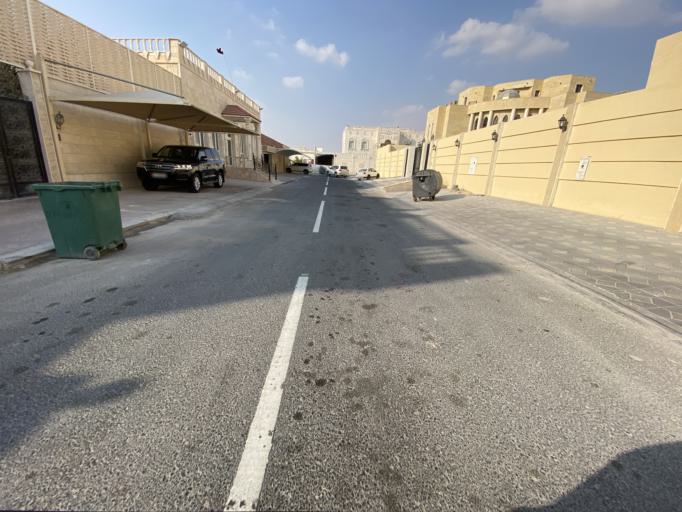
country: QA
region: Baladiyat ar Rayyan
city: Ar Rayyan
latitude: 25.2365
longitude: 51.3766
